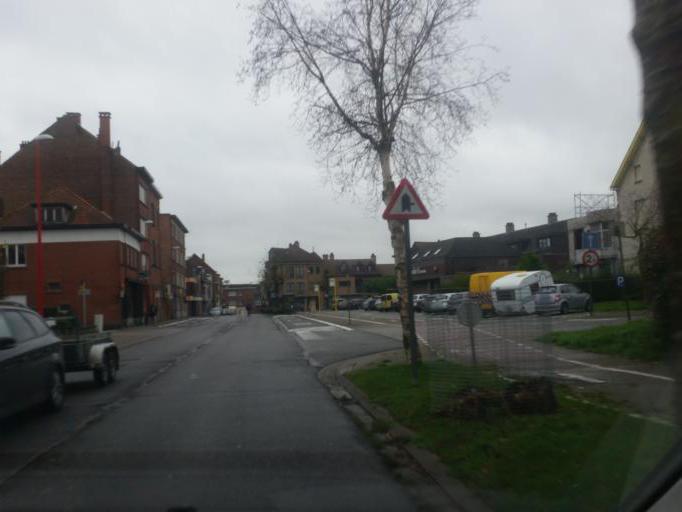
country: BE
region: Flanders
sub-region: Provincie Vlaams-Brabant
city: Grimbergen
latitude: 50.9133
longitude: 4.3576
